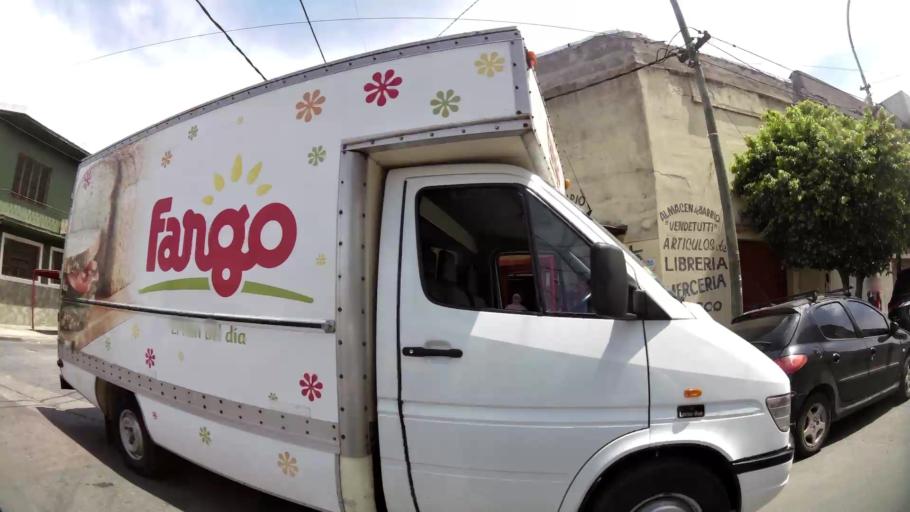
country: AR
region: Buenos Aires
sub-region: Partido de Lanus
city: Lanus
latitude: -34.6637
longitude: -58.4144
